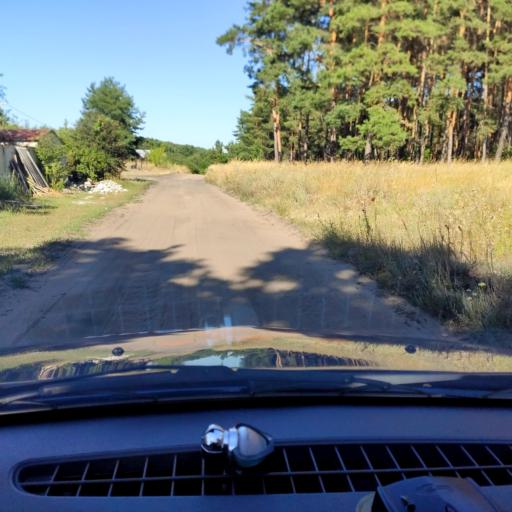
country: RU
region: Voronezj
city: Shilovo
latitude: 51.5397
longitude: 39.1611
